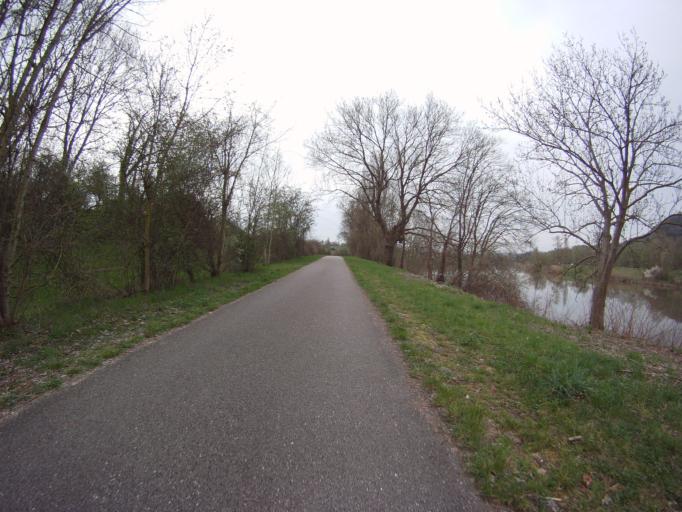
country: FR
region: Lorraine
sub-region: Departement de Meurthe-et-Moselle
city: Champigneulles
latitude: 48.7300
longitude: 6.1758
